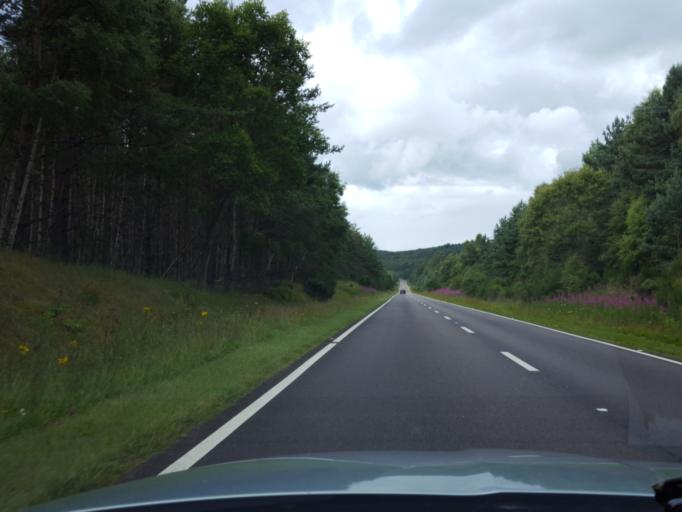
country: GB
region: Scotland
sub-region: Highland
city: Grantown on Spey
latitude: 57.2819
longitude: -3.6864
